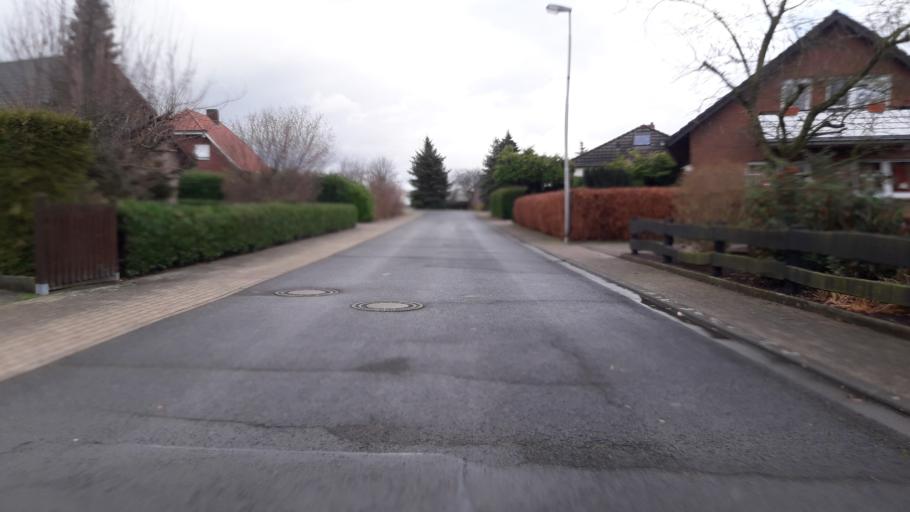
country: DE
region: North Rhine-Westphalia
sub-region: Regierungsbezirk Detmold
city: Petershagen
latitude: 52.3436
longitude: 8.9658
